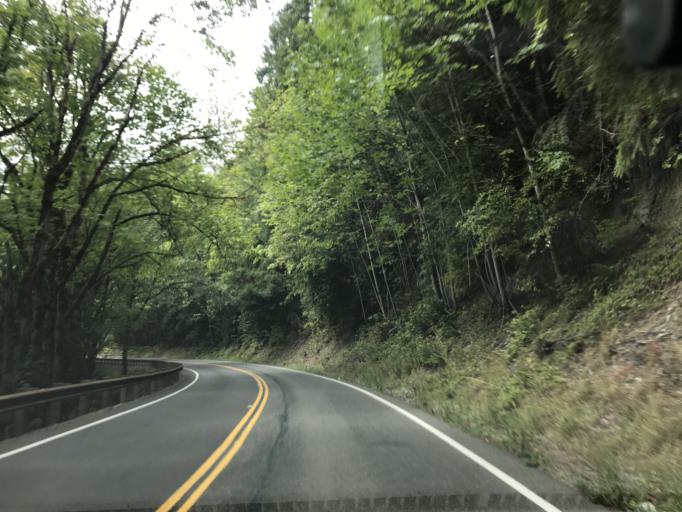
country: US
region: Washington
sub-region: King County
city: Black Diamond
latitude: 47.2861
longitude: -122.0291
